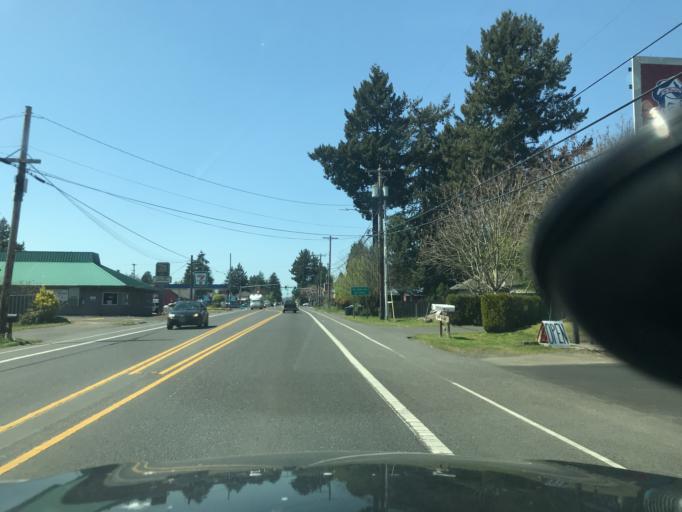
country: US
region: Oregon
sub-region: Multnomah County
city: Lents
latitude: 45.4968
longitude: -122.5458
